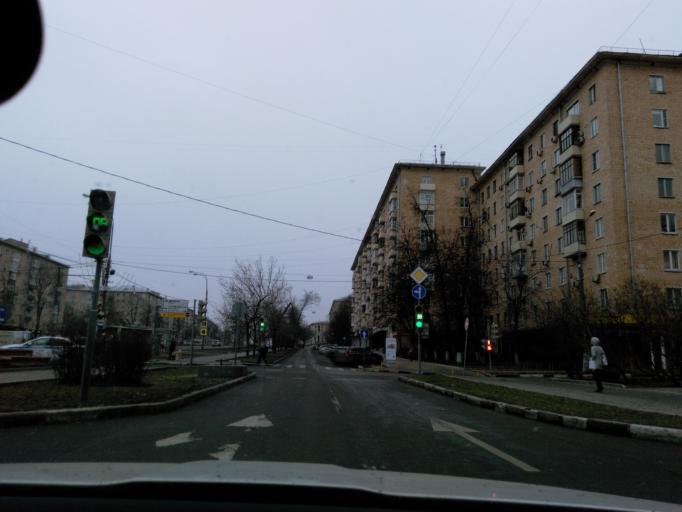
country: RU
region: Moskovskaya
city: Semenovskoye
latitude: 55.6918
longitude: 37.5508
